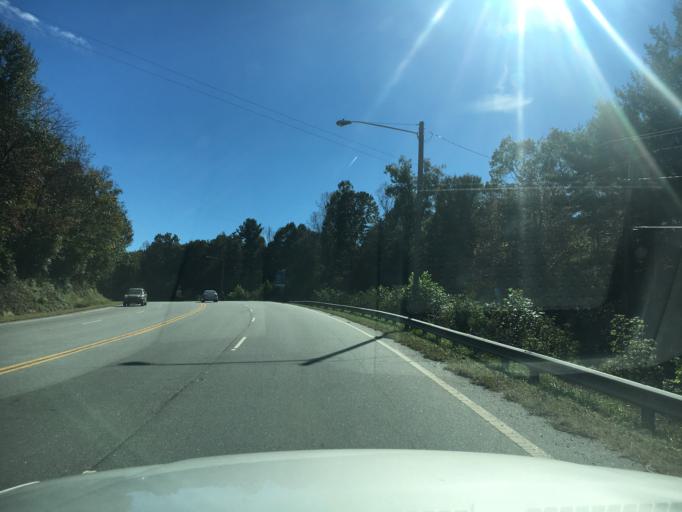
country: US
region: North Carolina
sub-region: Burke County
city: Morganton
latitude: 35.7682
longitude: -81.6921
